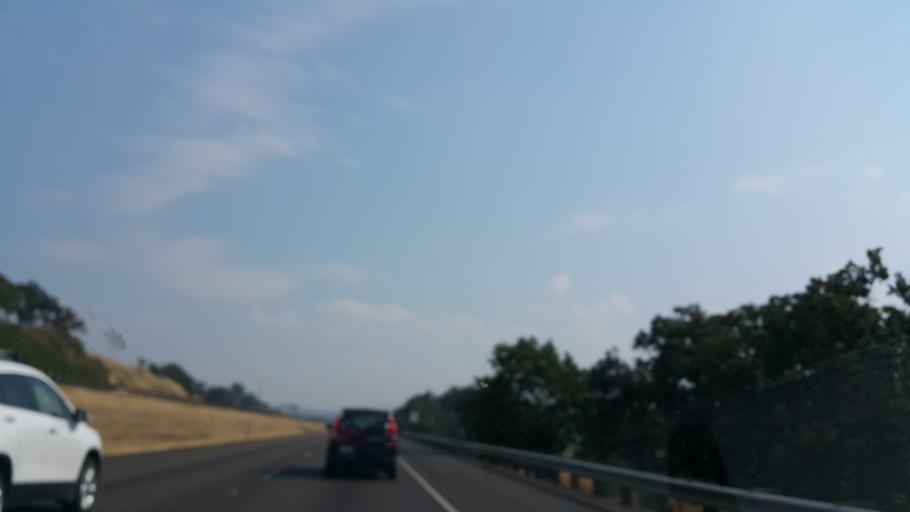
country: US
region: Oregon
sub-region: Jackson County
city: Phoenix
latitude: 42.3000
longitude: -122.8363
